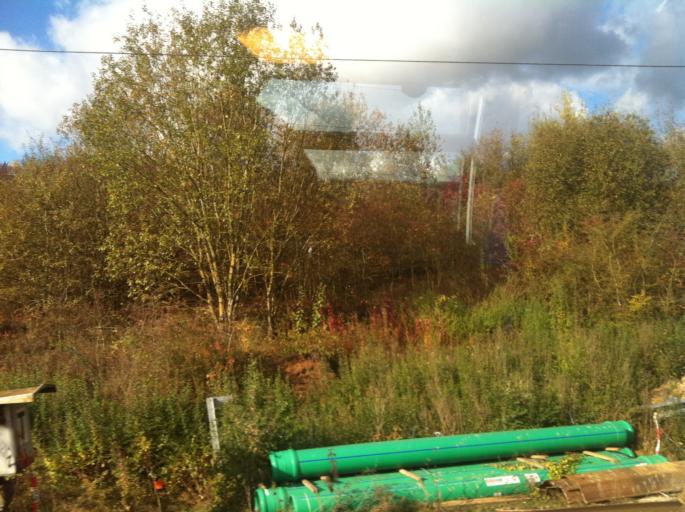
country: LU
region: Luxembourg
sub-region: Canton de Luxembourg
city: Hesperange
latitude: 49.5840
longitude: 6.1345
